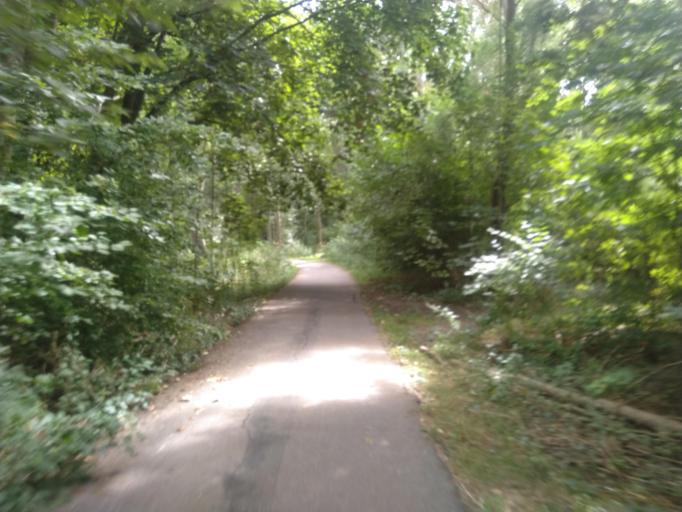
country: NL
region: North Holland
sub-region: Gemeente Zaanstad
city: Zaanstad
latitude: 52.3980
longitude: 4.7385
